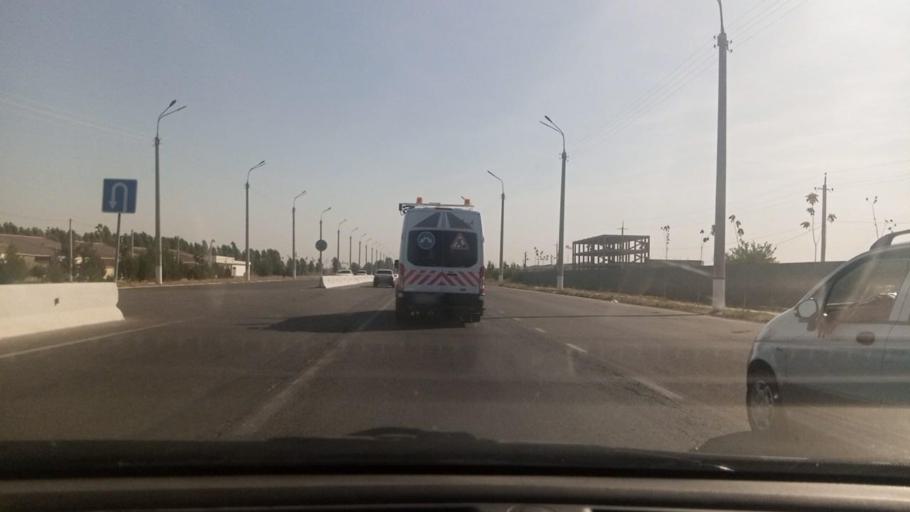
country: UZ
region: Toshkent Shahri
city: Bektemir
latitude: 41.2045
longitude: 69.3359
